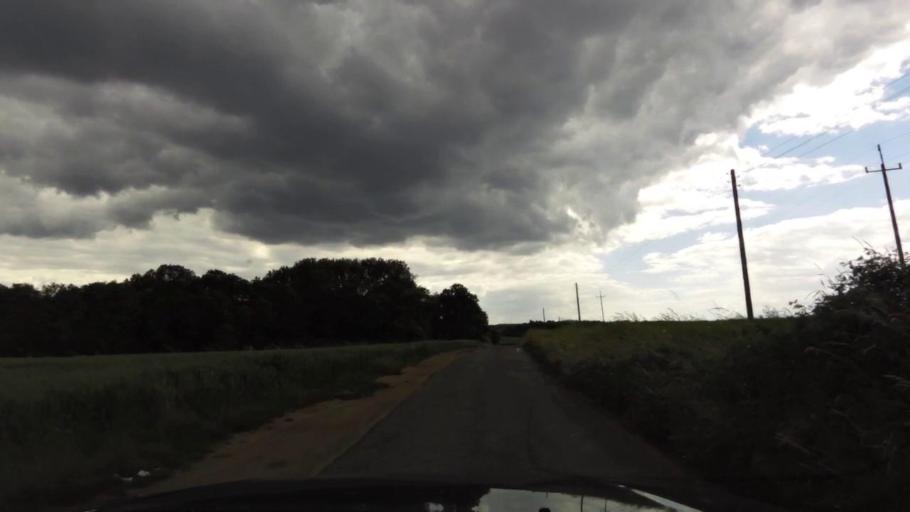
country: PL
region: West Pomeranian Voivodeship
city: Trzcinsko Zdroj
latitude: 52.9378
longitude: 14.5971
